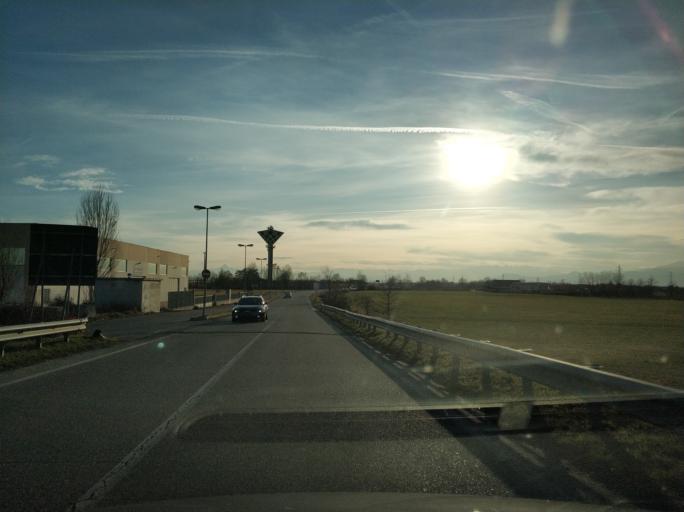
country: IT
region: Piedmont
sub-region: Provincia di Torino
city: Brandizzo
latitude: 45.1858
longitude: 7.8339
